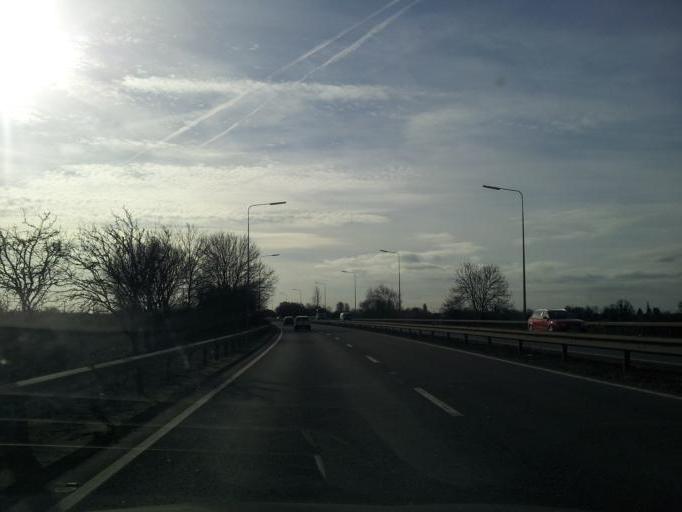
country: GB
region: England
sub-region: Central Bedfordshire
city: Biggleswade
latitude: 52.0831
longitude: -0.2735
